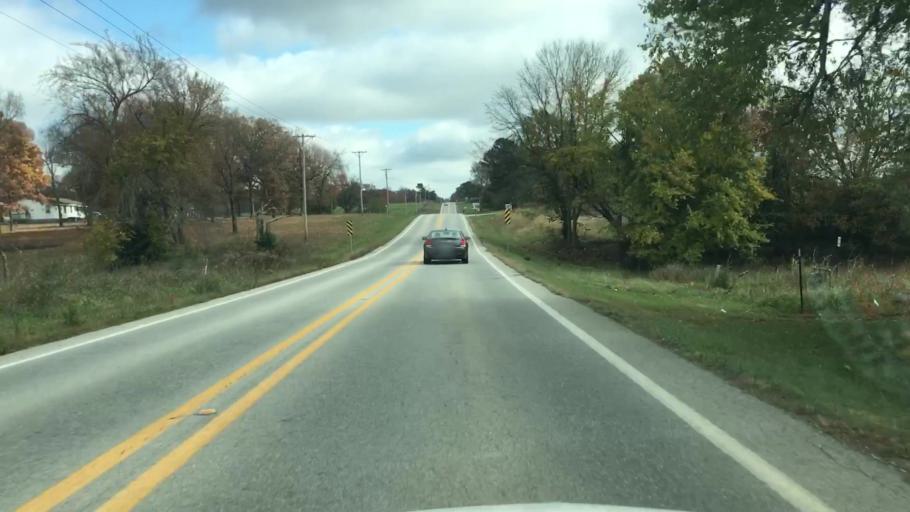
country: US
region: Arkansas
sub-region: Benton County
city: Gentry
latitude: 36.2634
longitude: -94.4613
